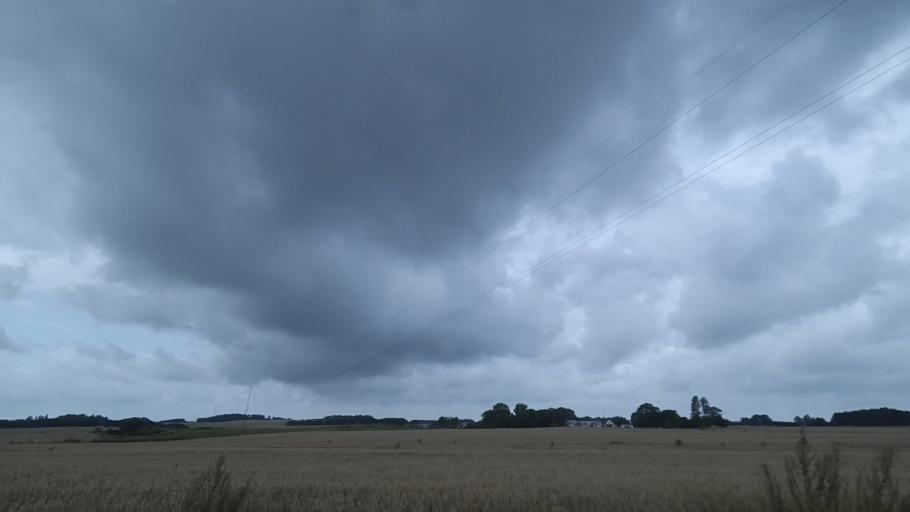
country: DK
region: Central Jutland
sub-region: Syddjurs Kommune
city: Ryomgard
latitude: 56.3880
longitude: 10.5665
